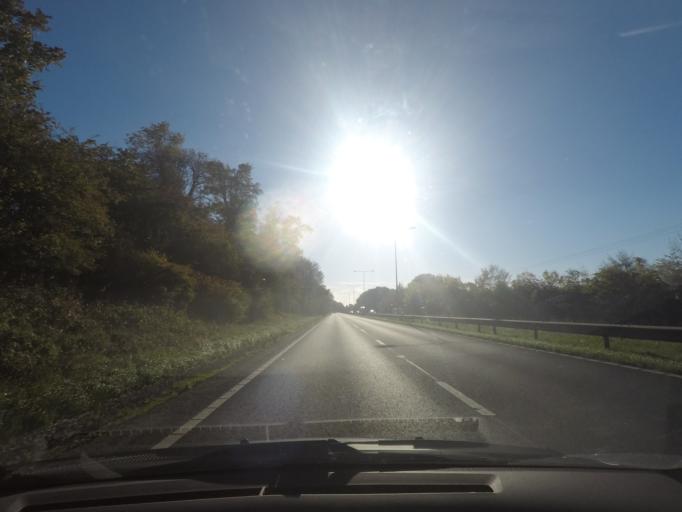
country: GB
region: England
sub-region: East Riding of Yorkshire
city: Brantingham
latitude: 53.7469
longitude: -0.5722
